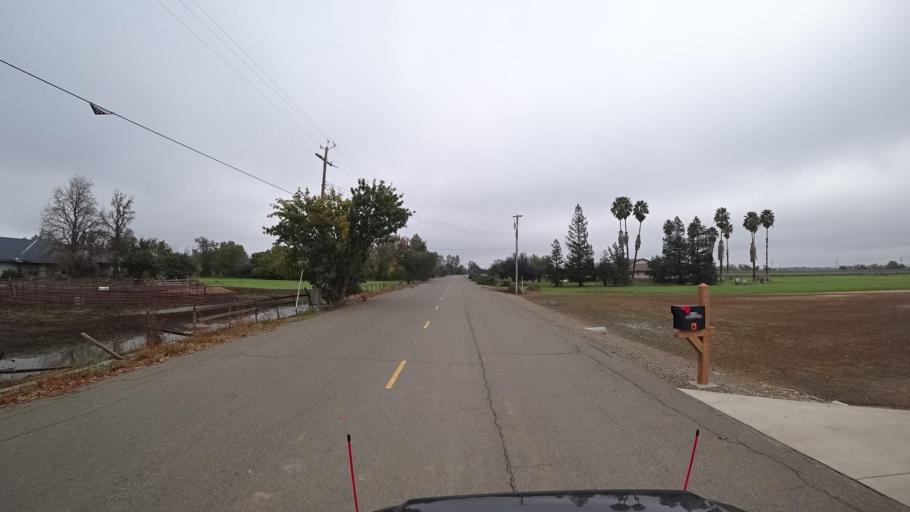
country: US
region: California
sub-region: Sacramento County
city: Elk Grove
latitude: 38.4135
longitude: -121.3259
